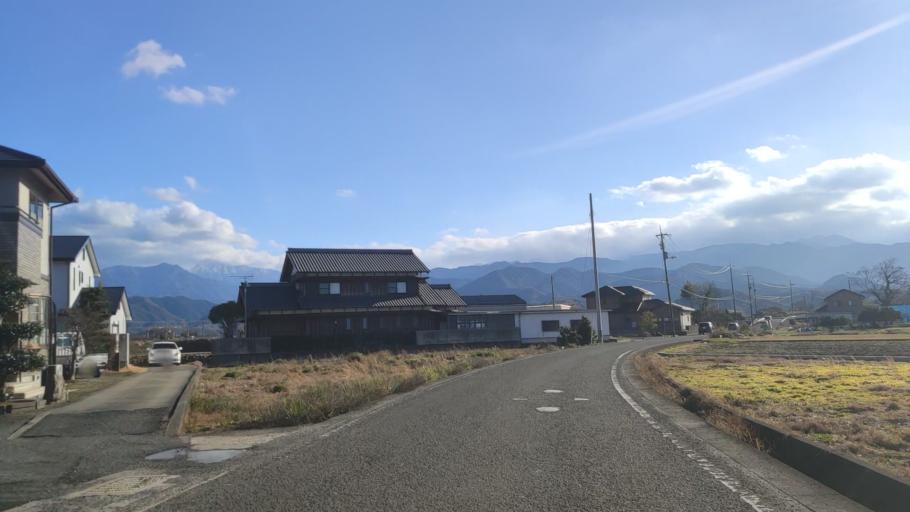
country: JP
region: Ehime
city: Saijo
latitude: 33.9106
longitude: 133.0973
